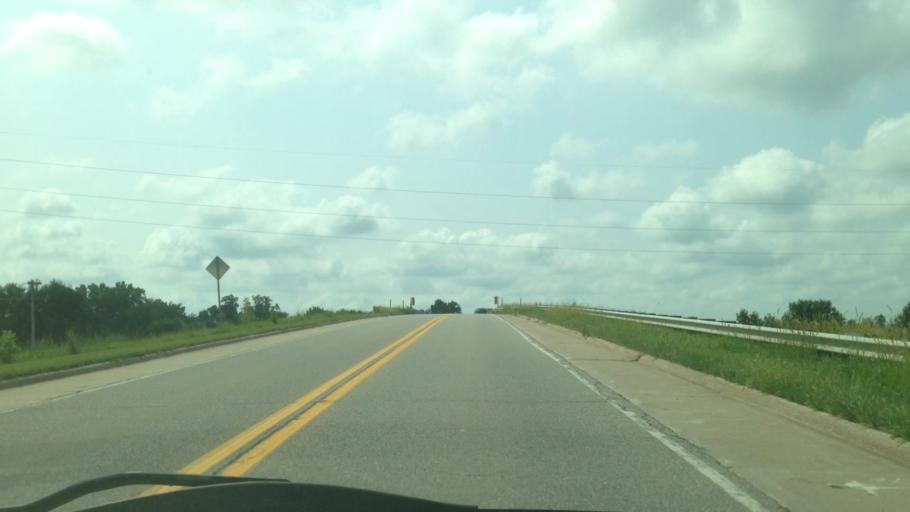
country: US
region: Iowa
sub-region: Linn County
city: Fairfax
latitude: 41.9216
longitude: -91.7838
